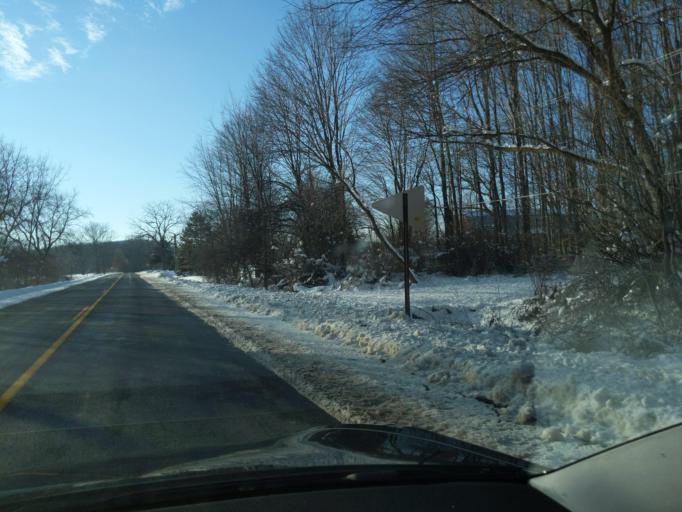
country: US
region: Michigan
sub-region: Ingham County
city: Stockbridge
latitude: 42.4316
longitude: -84.0831
